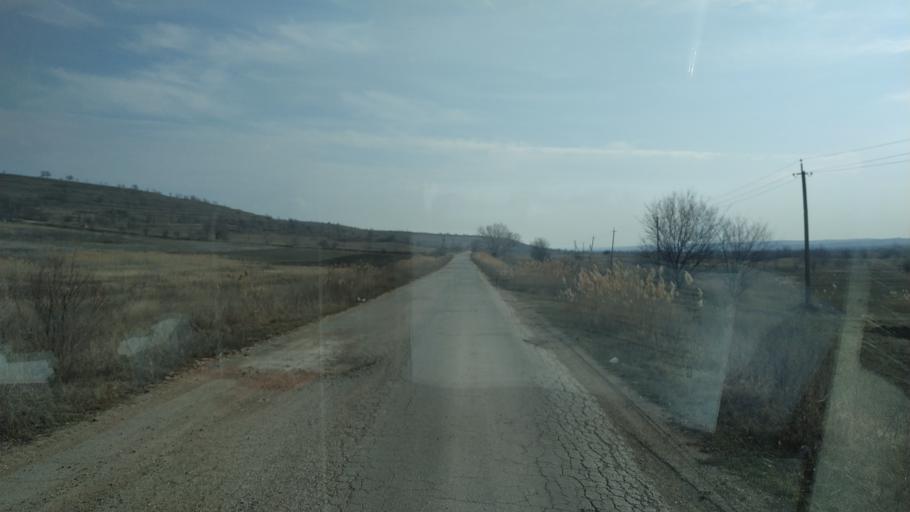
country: MD
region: Chisinau
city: Singera
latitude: 46.9255
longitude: 29.0785
